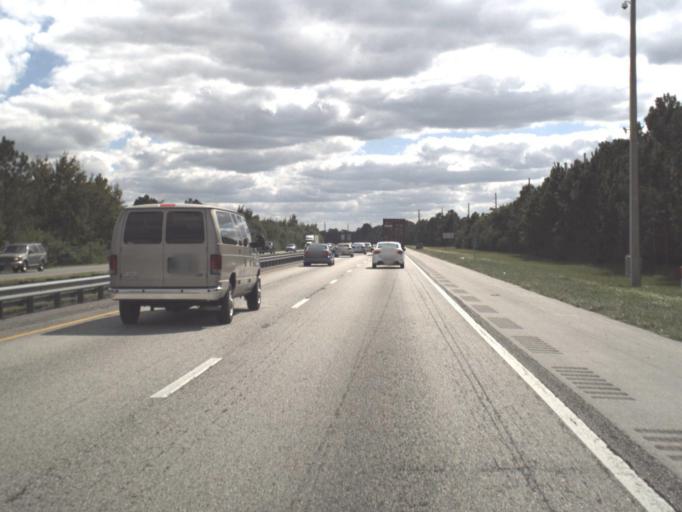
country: US
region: Florida
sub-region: Osceola County
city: Buenaventura Lakes
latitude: 28.3183
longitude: -81.3714
